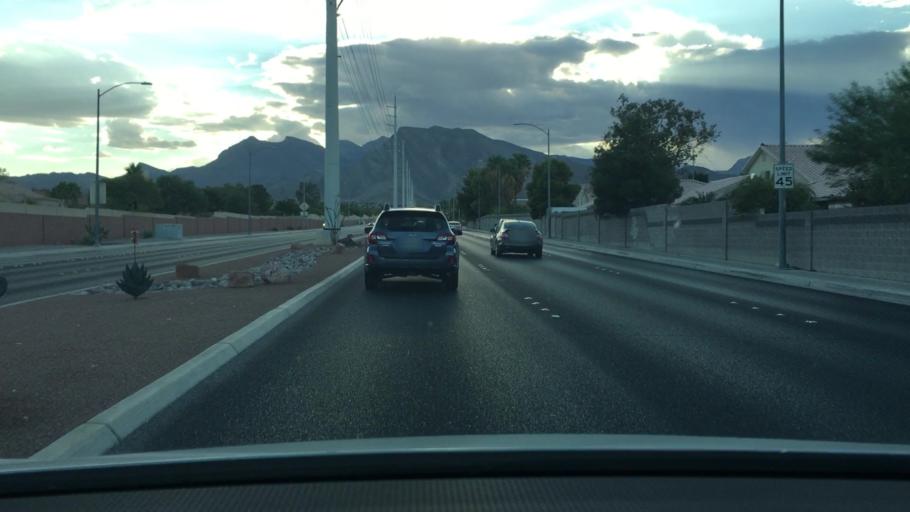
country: US
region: Nevada
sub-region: Clark County
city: Summerlin South
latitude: 36.2186
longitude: -115.2892
